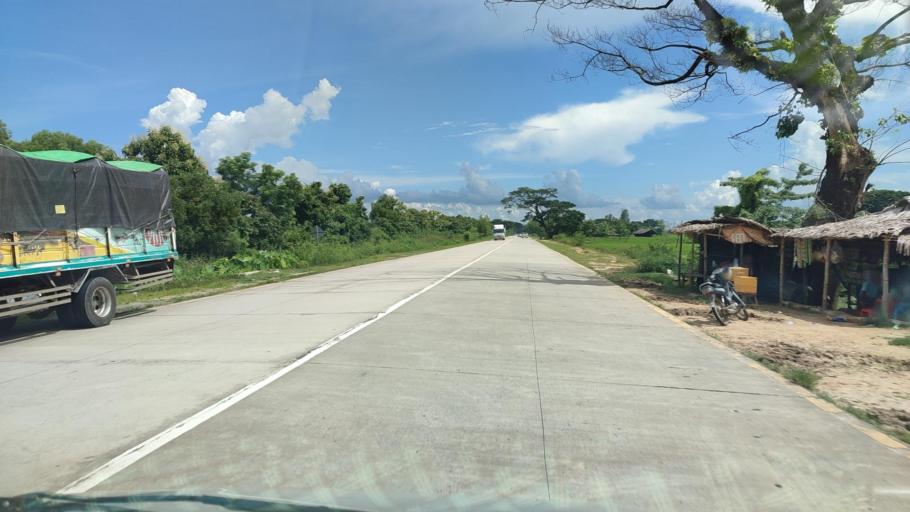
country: MM
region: Bago
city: Nyaunglebin
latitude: 17.9750
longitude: 96.7095
